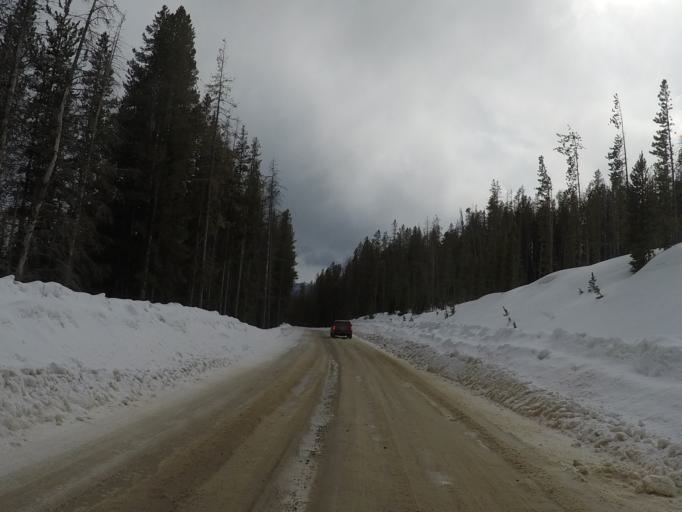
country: US
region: Montana
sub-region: Granite County
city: Philipsburg
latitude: 46.2272
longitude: -113.2502
